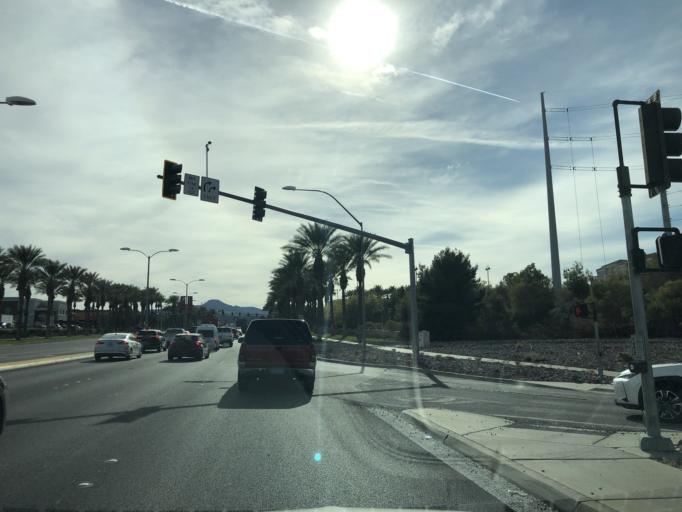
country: US
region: Nevada
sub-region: Clark County
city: Whitney
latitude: 36.0241
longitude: -115.0848
